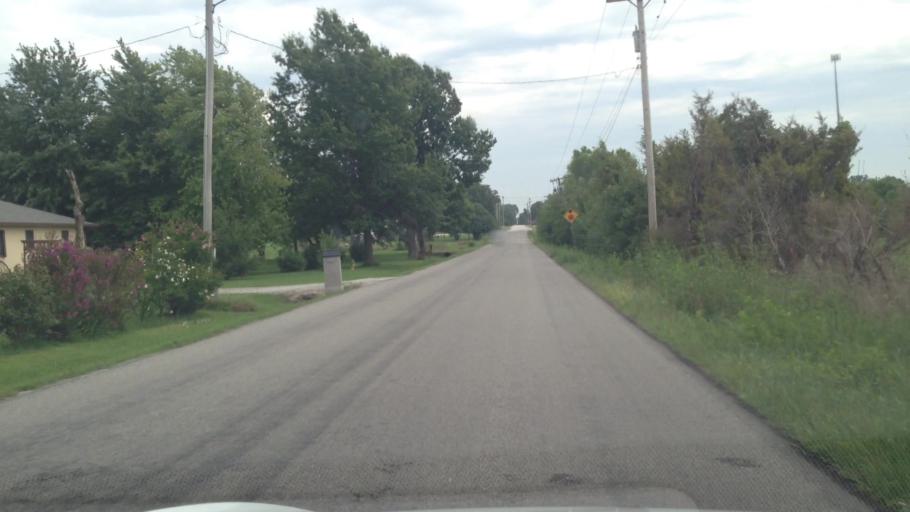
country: US
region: Kansas
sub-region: Crawford County
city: Girard
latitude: 37.4992
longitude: -94.8464
